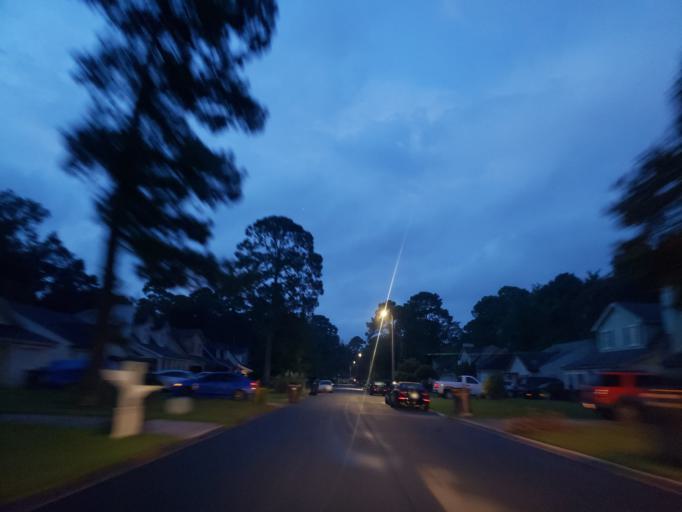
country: US
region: Georgia
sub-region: Chatham County
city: Isle of Hope
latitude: 31.9930
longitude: -81.0739
